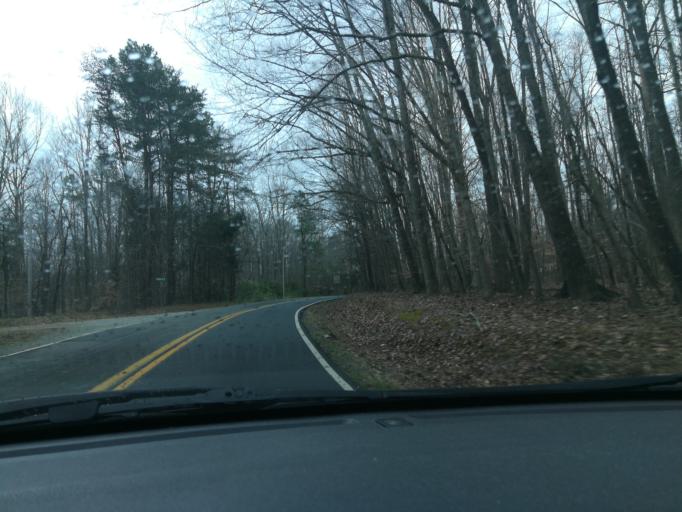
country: US
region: North Carolina
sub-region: Orange County
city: Hillsborough
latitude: 36.0263
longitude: -79.0606
